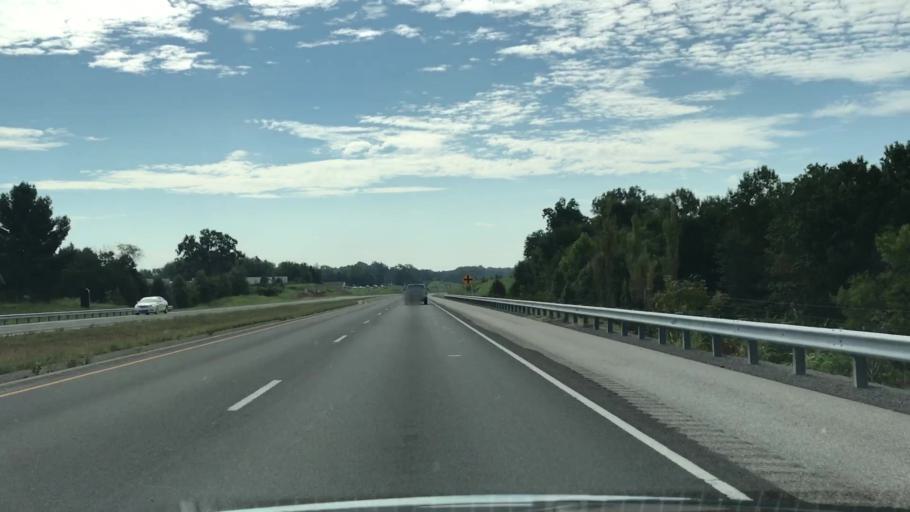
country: US
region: Kentucky
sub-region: Warren County
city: Plano
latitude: 36.8377
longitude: -86.3201
